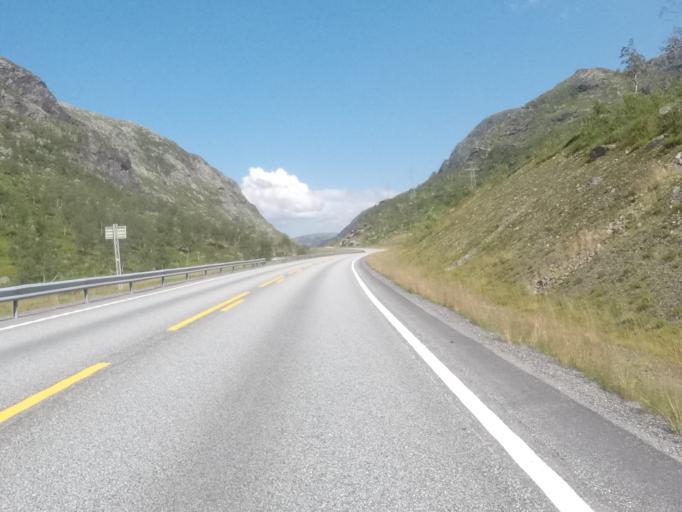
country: NO
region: Hordaland
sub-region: Modalen
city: Mo
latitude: 60.8039
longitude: 5.6173
